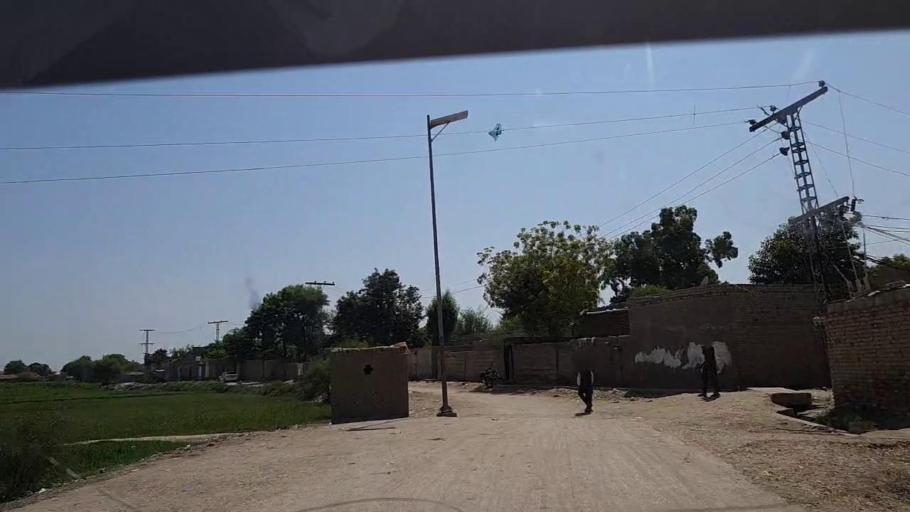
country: PK
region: Sindh
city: Ghauspur
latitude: 28.1408
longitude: 69.0880
